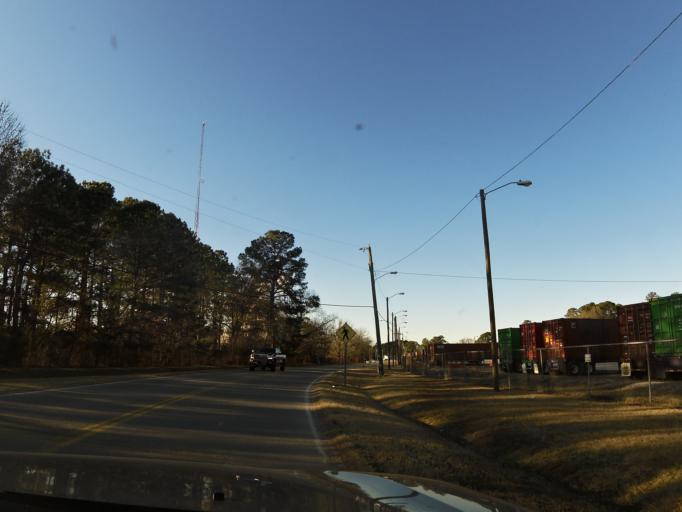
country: US
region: Virginia
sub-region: City of Franklin
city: Franklin
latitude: 36.6774
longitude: -76.9071
